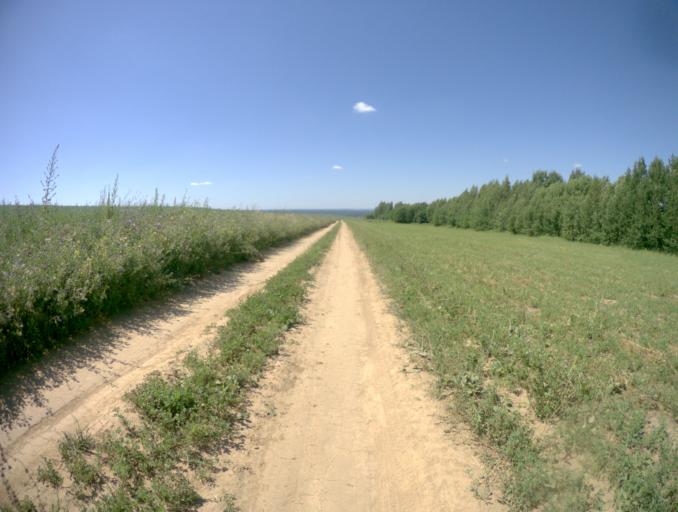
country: RU
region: Nizjnij Novgorod
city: Gorbatov
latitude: 56.1320
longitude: 43.0340
